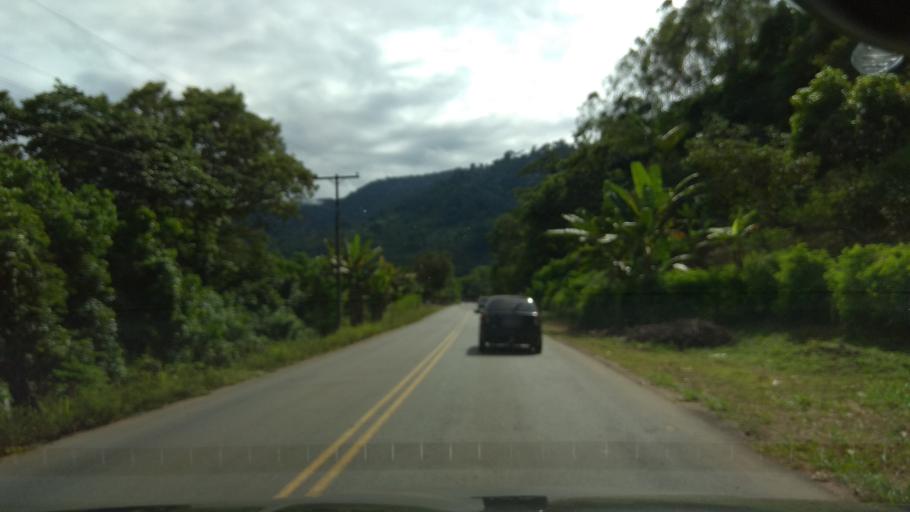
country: BR
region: Bahia
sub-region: Ubaira
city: Ubaira
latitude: -13.2622
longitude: -39.6182
